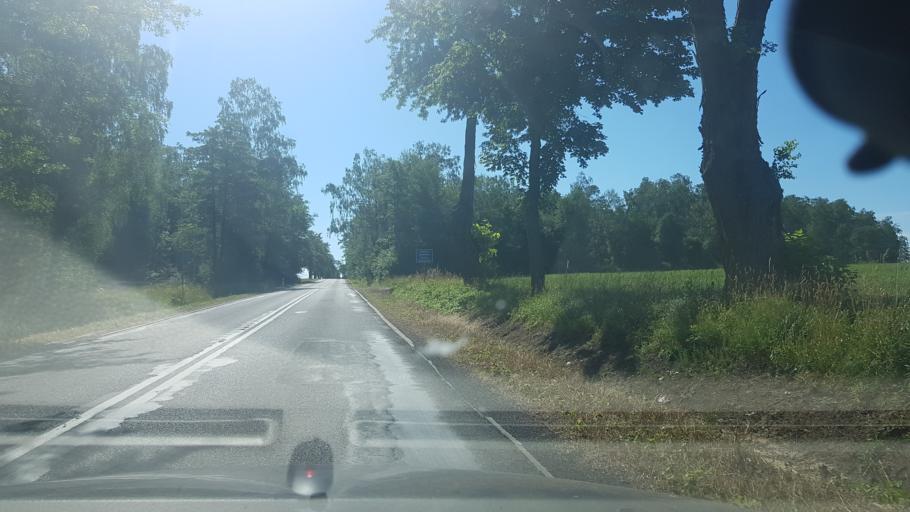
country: PL
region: Masovian Voivodeship
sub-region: Powiat siedlecki
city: Mokobody
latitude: 52.3120
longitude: 22.0942
